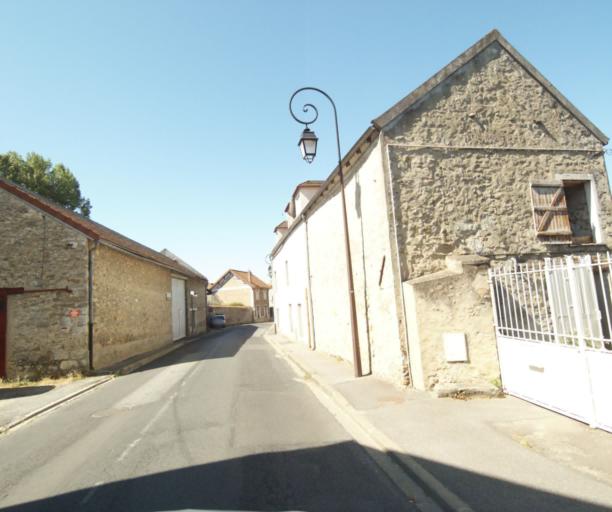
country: FR
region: Ile-de-France
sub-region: Departement de l'Essonne
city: Itteville
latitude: 48.5160
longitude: 2.3445
